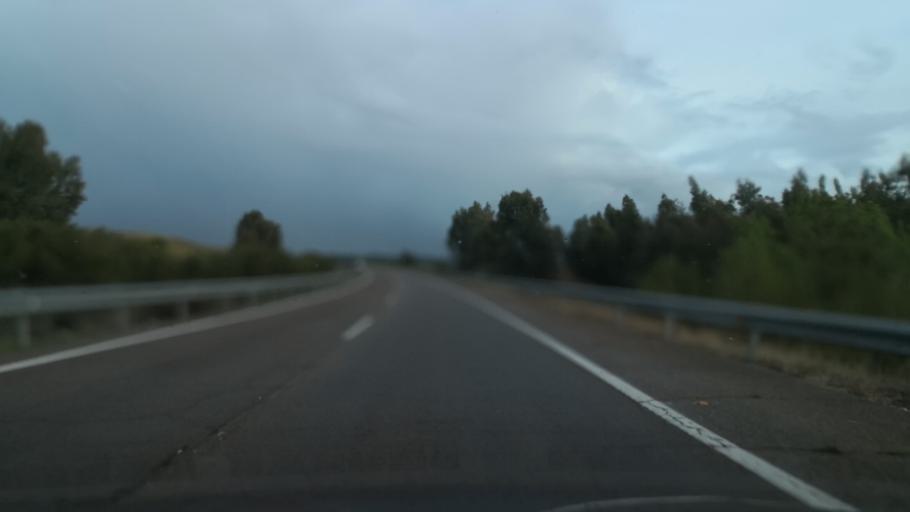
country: ES
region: Extremadura
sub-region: Provincia de Badajoz
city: Badajoz
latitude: 38.9134
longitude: -6.9495
